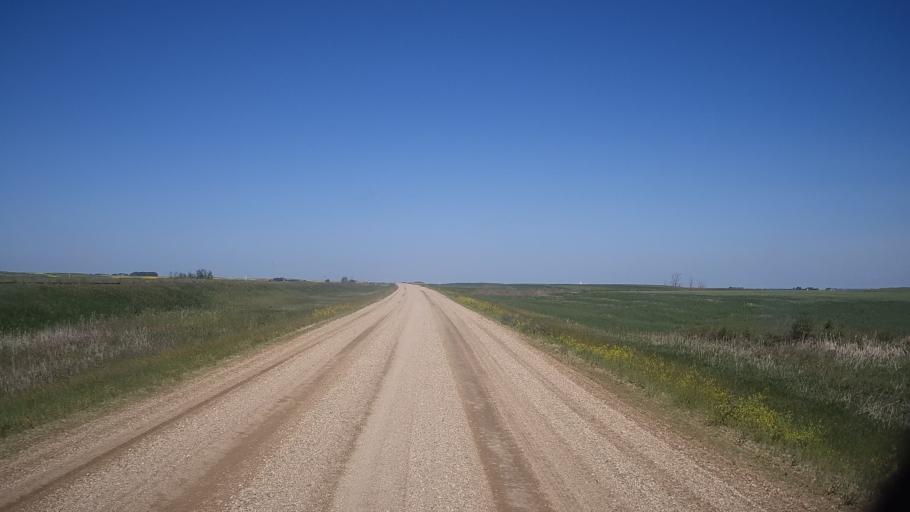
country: CA
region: Saskatchewan
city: Watrous
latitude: 51.8456
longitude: -105.9203
